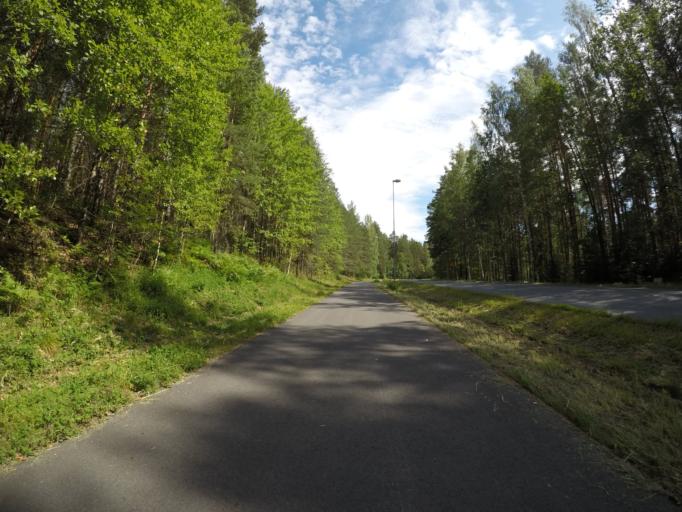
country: FI
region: Haeme
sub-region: Haemeenlinna
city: Haemeenlinna
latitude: 60.9948
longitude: 24.4033
